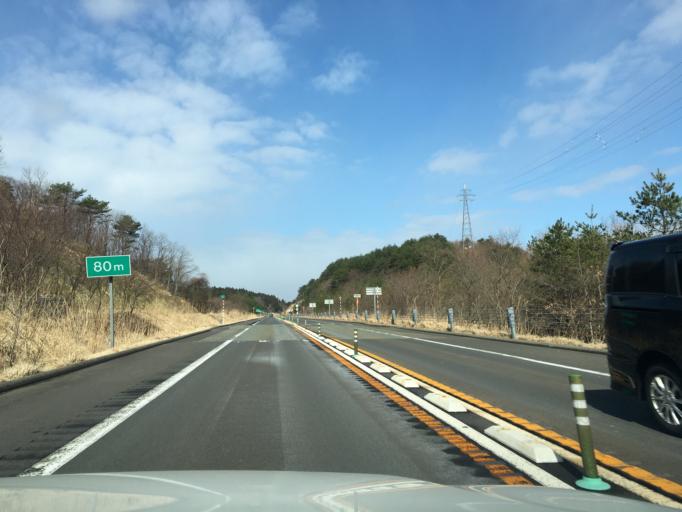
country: JP
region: Akita
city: Akita
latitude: 39.7597
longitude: 140.1318
